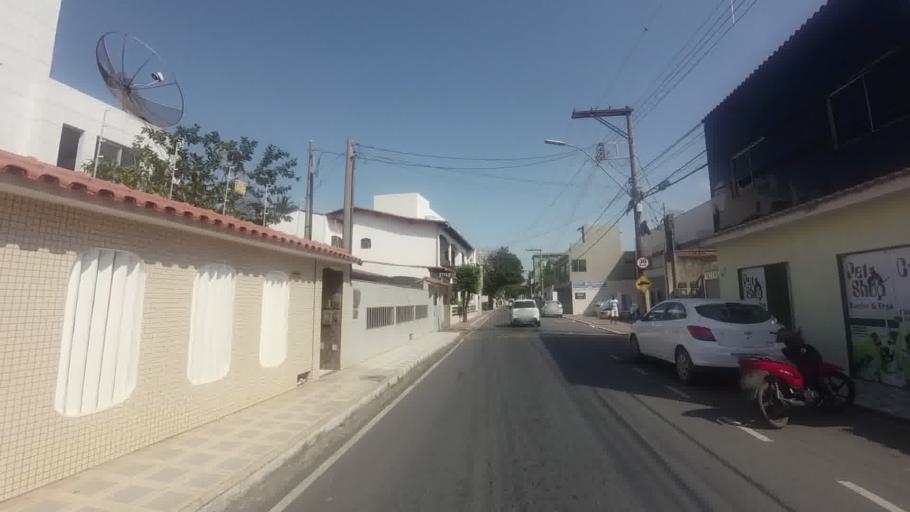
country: BR
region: Espirito Santo
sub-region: Piuma
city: Piuma
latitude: -20.8076
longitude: -40.6456
